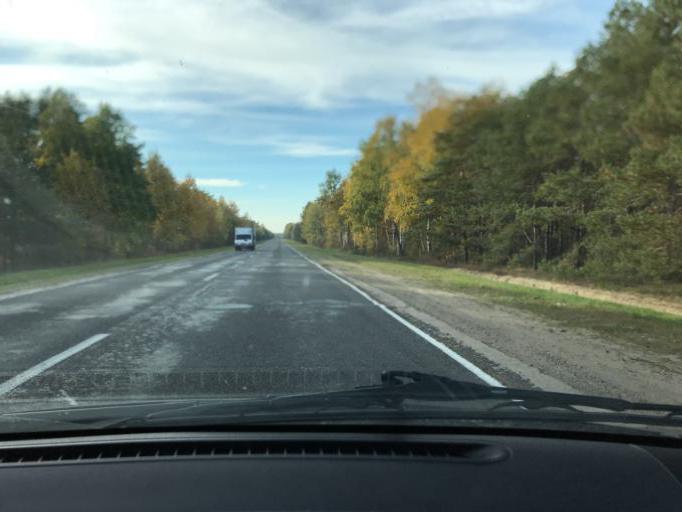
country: BY
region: Brest
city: Ivanava
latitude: 52.1552
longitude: 25.7897
